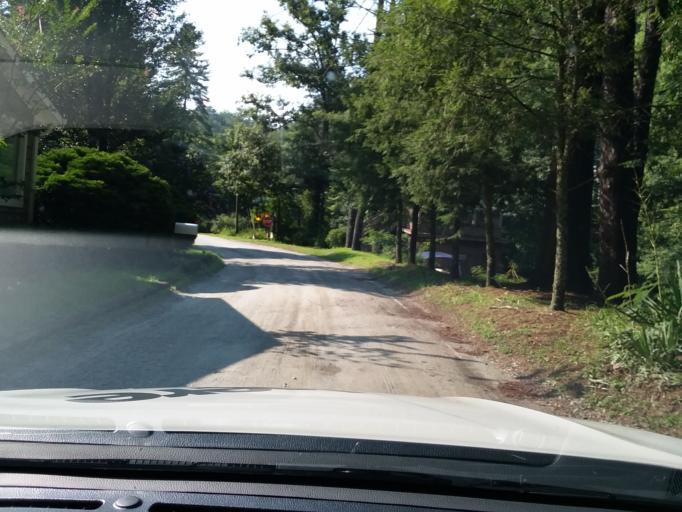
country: US
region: Georgia
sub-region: Habersham County
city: Clarkesville
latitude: 34.7555
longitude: -83.4963
